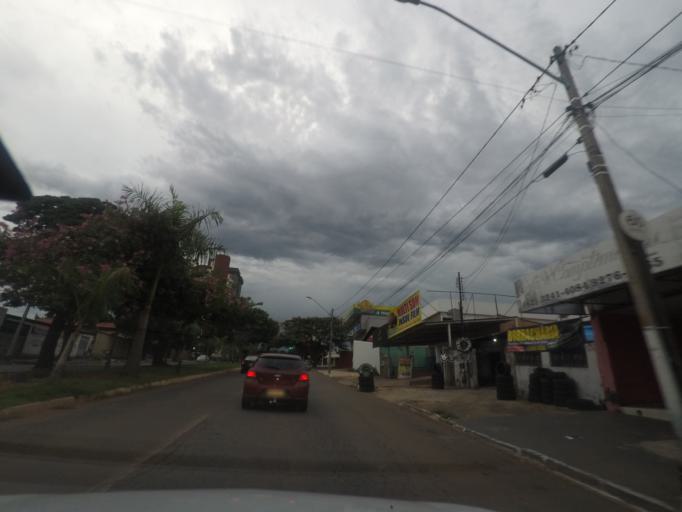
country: BR
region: Goias
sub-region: Goiania
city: Goiania
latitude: -16.7125
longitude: -49.2460
